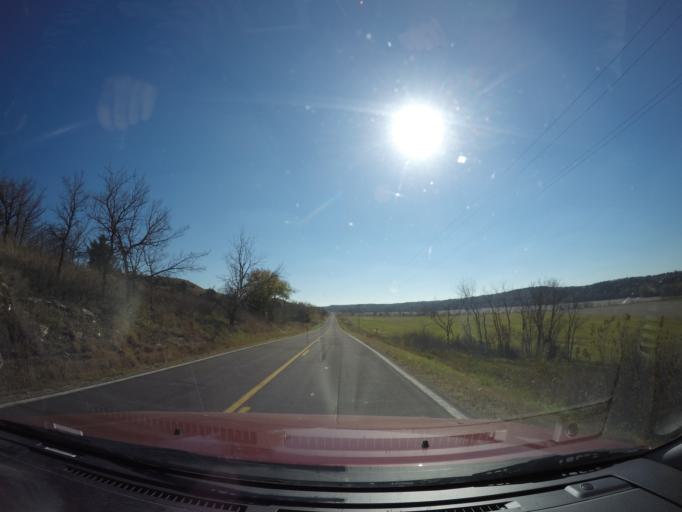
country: US
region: Kansas
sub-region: Geary County
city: Grandview Plaza
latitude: 38.9940
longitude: -96.7300
